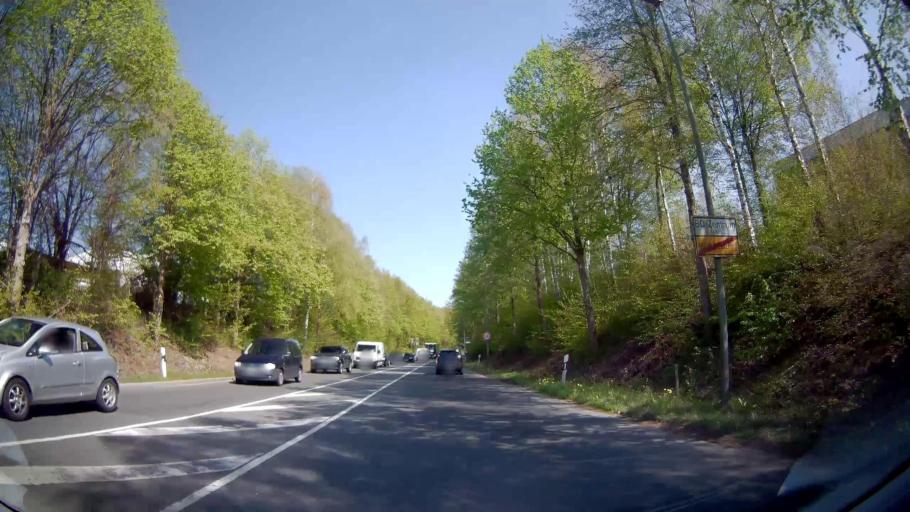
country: DE
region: North Rhine-Westphalia
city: Bochum-Hordel
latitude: 51.4864
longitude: 7.1664
